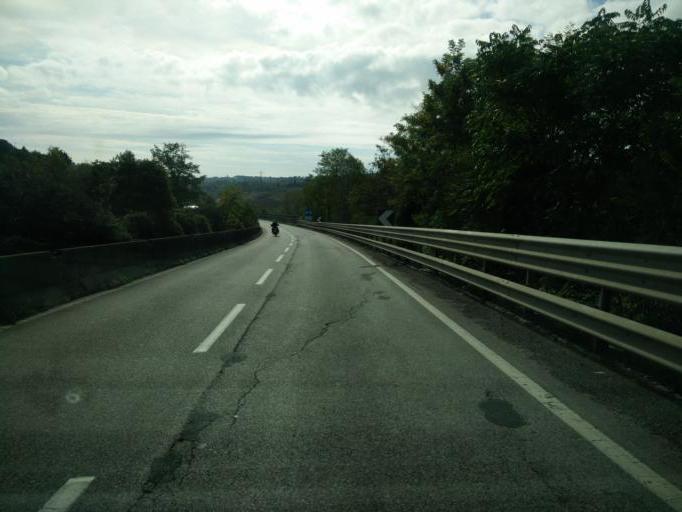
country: IT
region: Tuscany
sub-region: Provincia di Siena
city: Belverde
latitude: 43.3326
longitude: 11.2915
